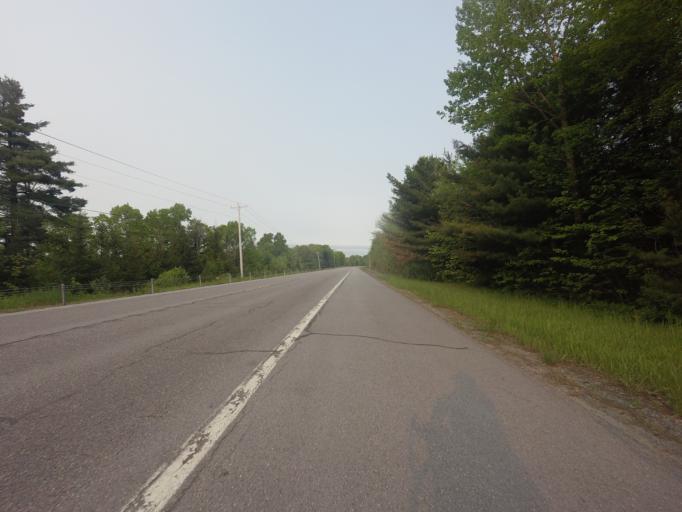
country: US
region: New York
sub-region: Jefferson County
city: Carthage
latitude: 44.0750
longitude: -75.4540
